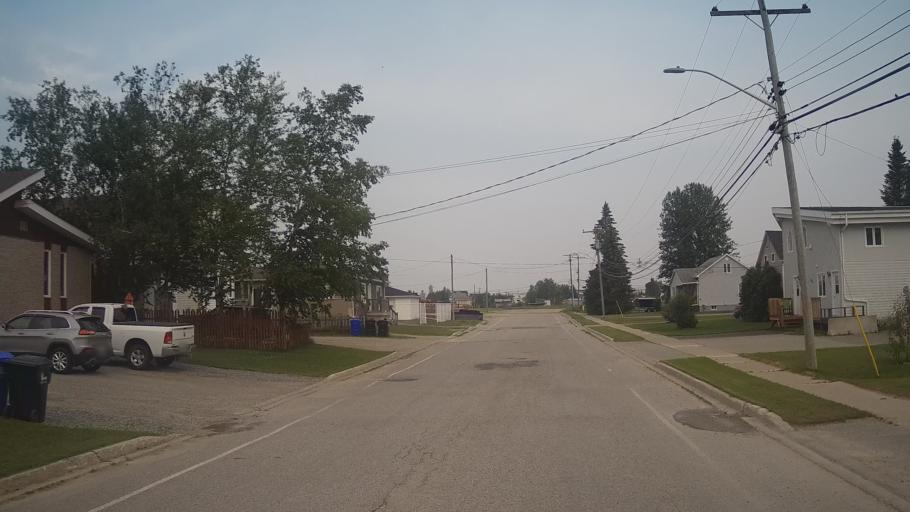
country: CA
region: Ontario
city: Hearst
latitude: 49.6896
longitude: -83.6520
